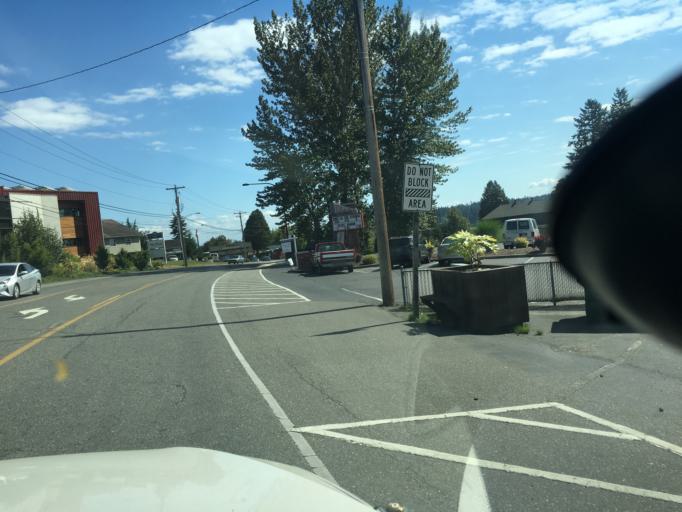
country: US
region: Washington
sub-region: Kitsap County
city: Kingston
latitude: 47.8008
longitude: -122.4993
